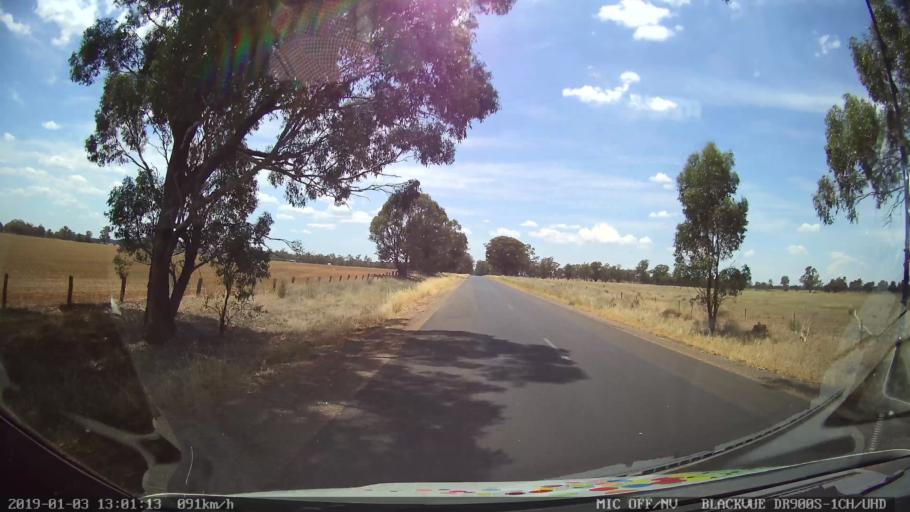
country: AU
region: New South Wales
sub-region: Cabonne
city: Canowindra
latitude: -33.6261
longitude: 148.4150
